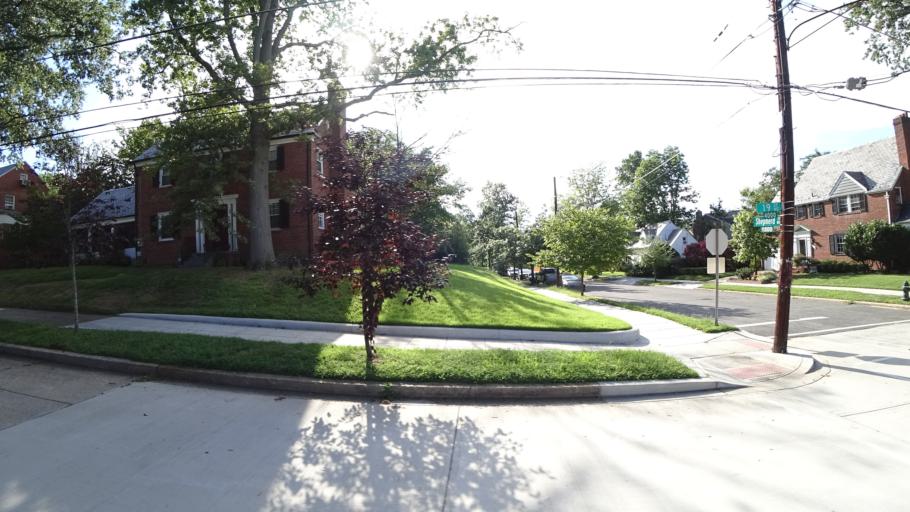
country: US
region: Maryland
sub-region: Prince George's County
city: Mount Rainier
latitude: 38.9395
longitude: -76.9783
